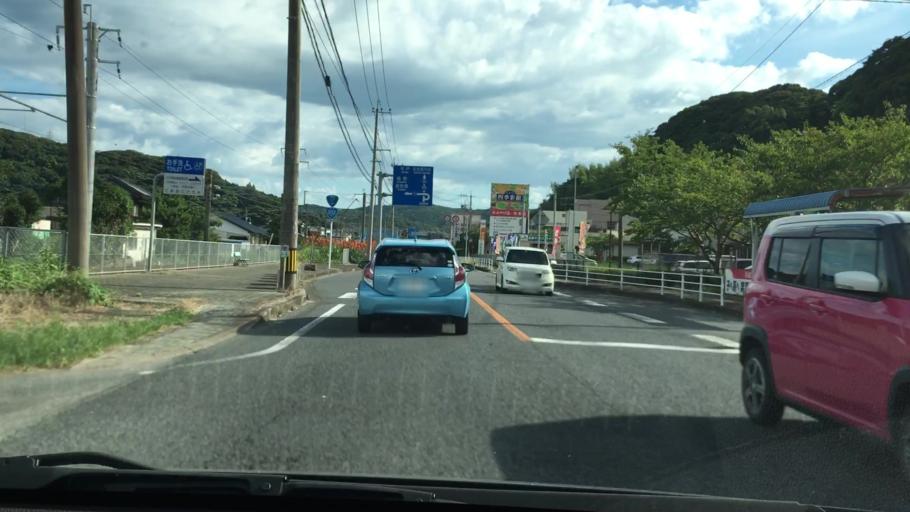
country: JP
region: Nagasaki
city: Sasebo
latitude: 33.1532
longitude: 129.8301
